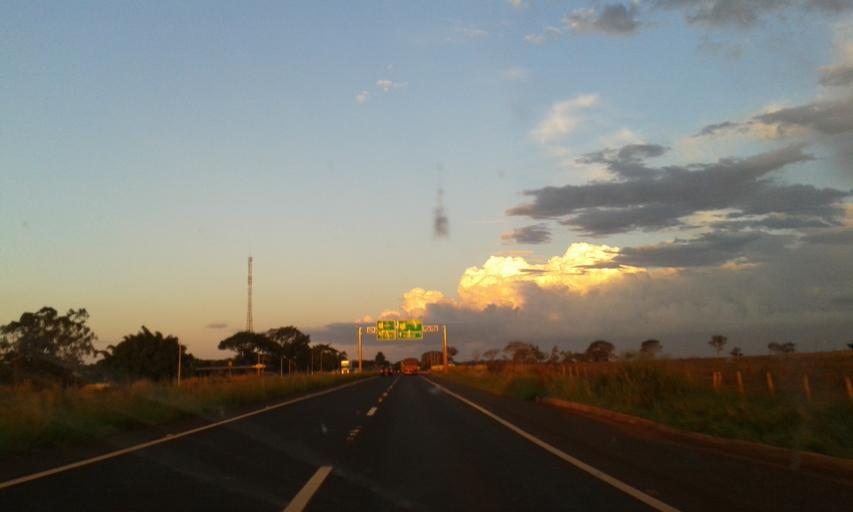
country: BR
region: Minas Gerais
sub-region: Monte Alegre De Minas
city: Monte Alegre de Minas
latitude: -18.8885
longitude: -48.7113
